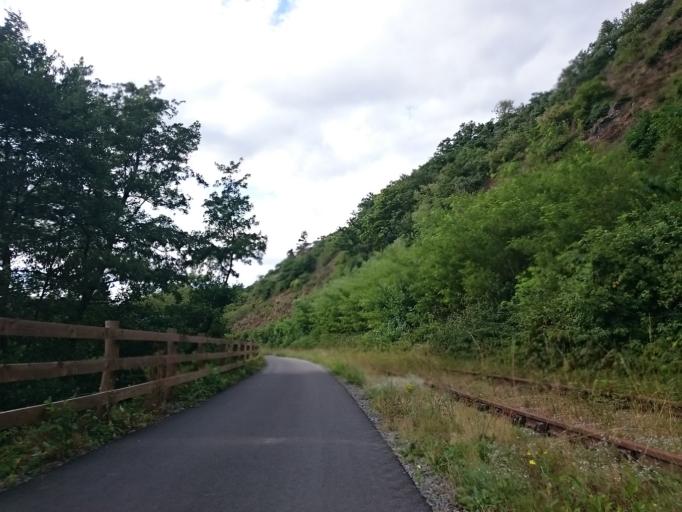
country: FR
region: Lower Normandy
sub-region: Departement du Calvados
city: Thury-Harcourt
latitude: 49.0049
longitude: -0.4654
